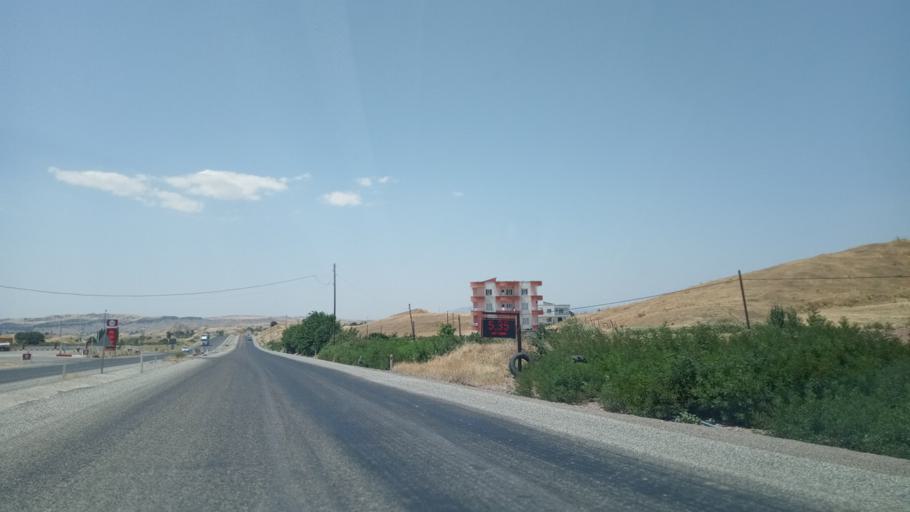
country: TR
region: Batman
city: Kozluk
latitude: 38.1719
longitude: 41.4412
